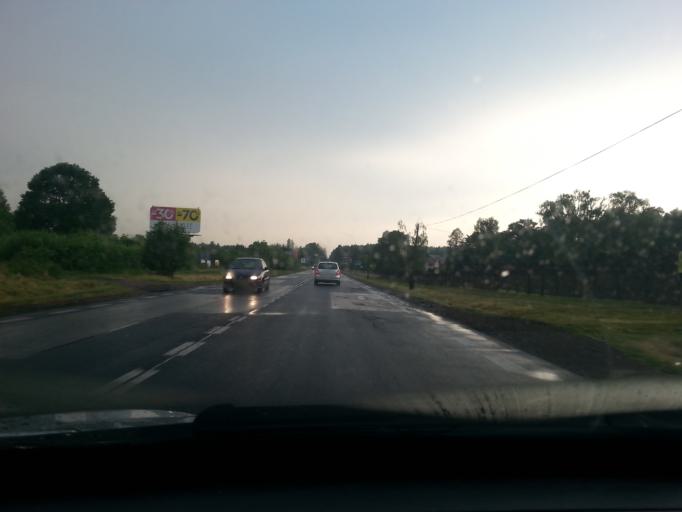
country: PL
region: Lodz Voivodeship
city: Lodz
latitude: 51.8274
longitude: 19.5253
